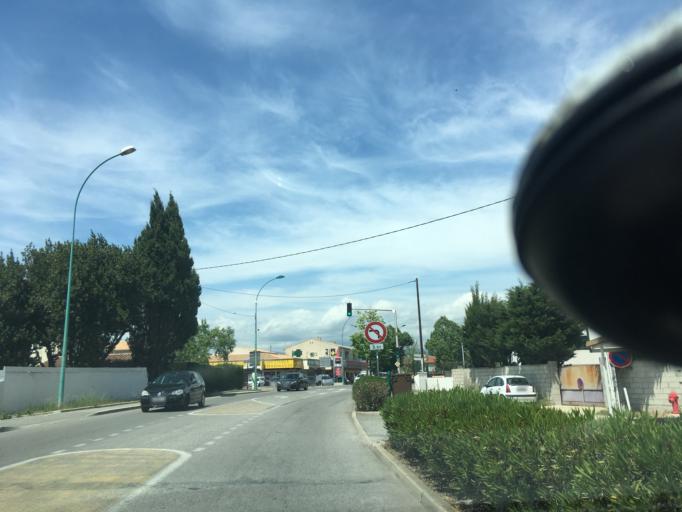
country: FR
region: Provence-Alpes-Cote d'Azur
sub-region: Departement du Var
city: Le Muy
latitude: 43.4723
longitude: 6.5610
